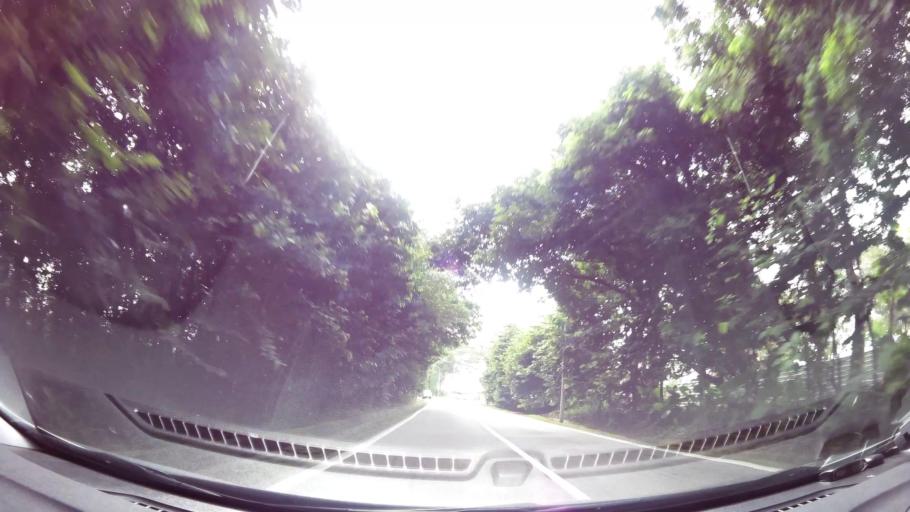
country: MY
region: Johor
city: Johor Bahru
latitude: 1.4374
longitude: 103.7281
